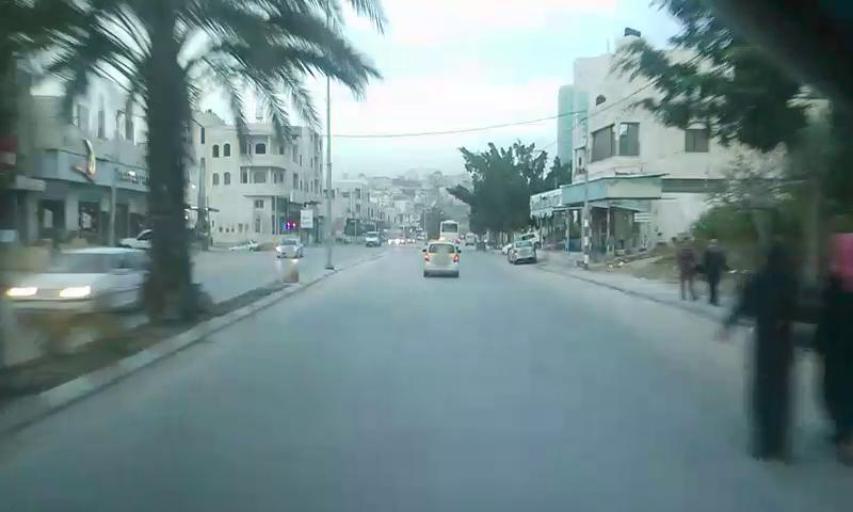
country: PS
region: West Bank
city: Dhannabah
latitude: 32.3189
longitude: 35.0405
